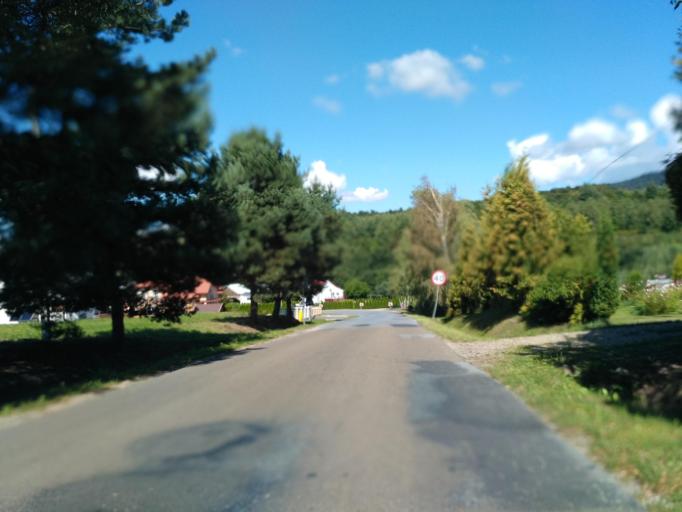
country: PL
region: Subcarpathian Voivodeship
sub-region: Powiat jasielski
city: Skolyszyn
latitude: 49.7898
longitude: 21.3416
